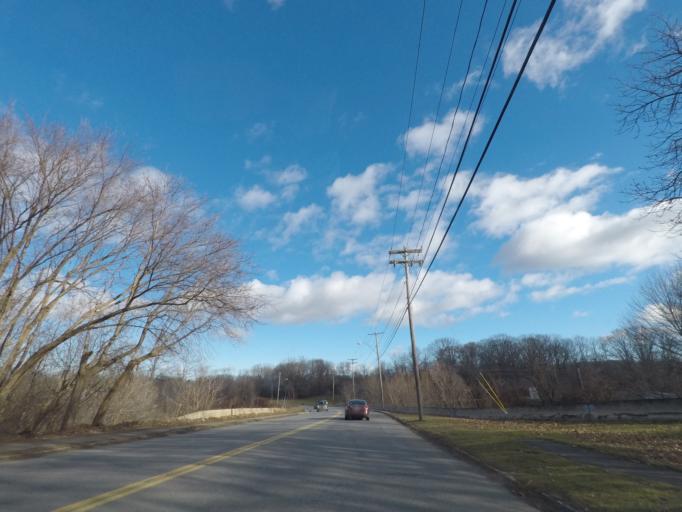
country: US
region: New York
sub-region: Albany County
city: Green Island
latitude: 42.7479
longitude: -73.6725
